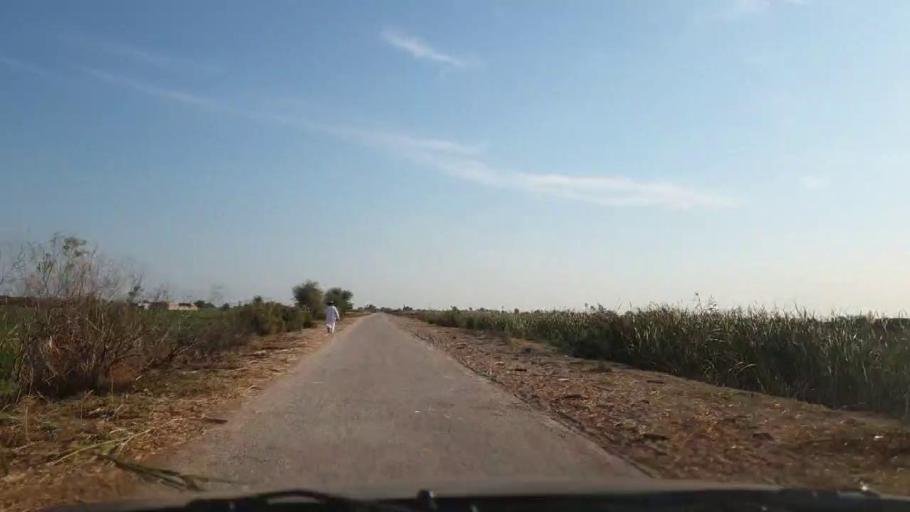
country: PK
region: Sindh
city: Khadro
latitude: 26.2097
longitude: 68.7450
